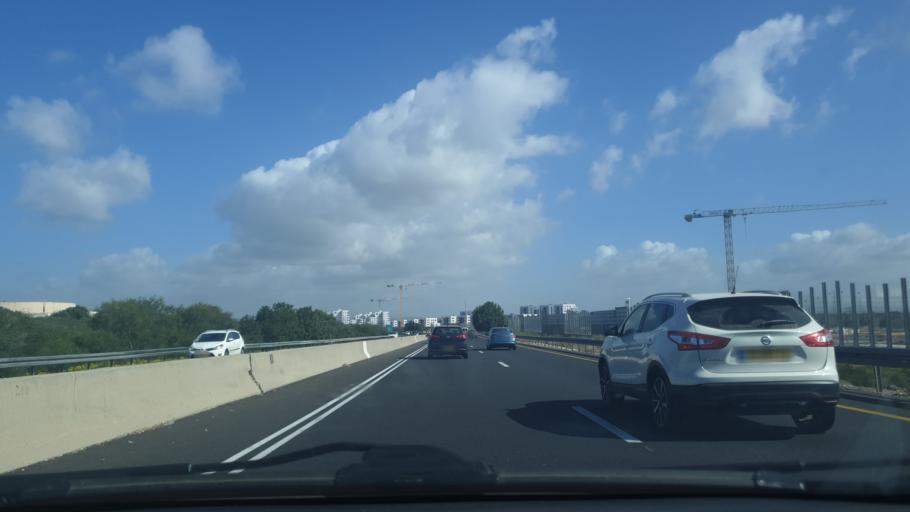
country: IL
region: Haifa
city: Qesarya
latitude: 32.4859
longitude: 34.9143
